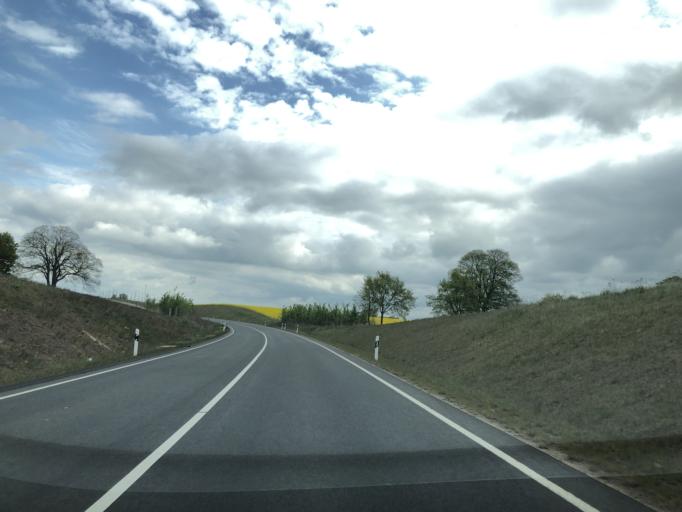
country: DE
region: Mecklenburg-Vorpommern
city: Plau am See
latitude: 53.4618
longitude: 12.2458
